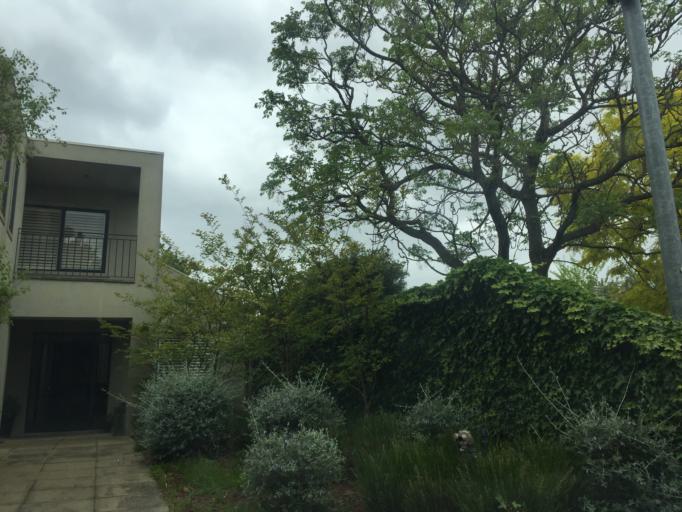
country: AU
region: Victoria
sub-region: Boroondara
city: Kew
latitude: -37.8066
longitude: 145.0408
